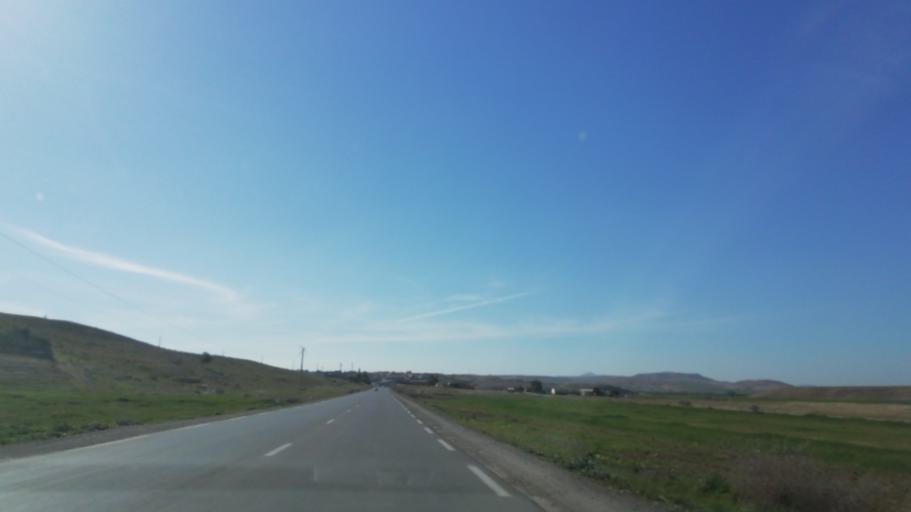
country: DZ
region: Mascara
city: Oued el Abtal
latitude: 35.4555
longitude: 0.7315
